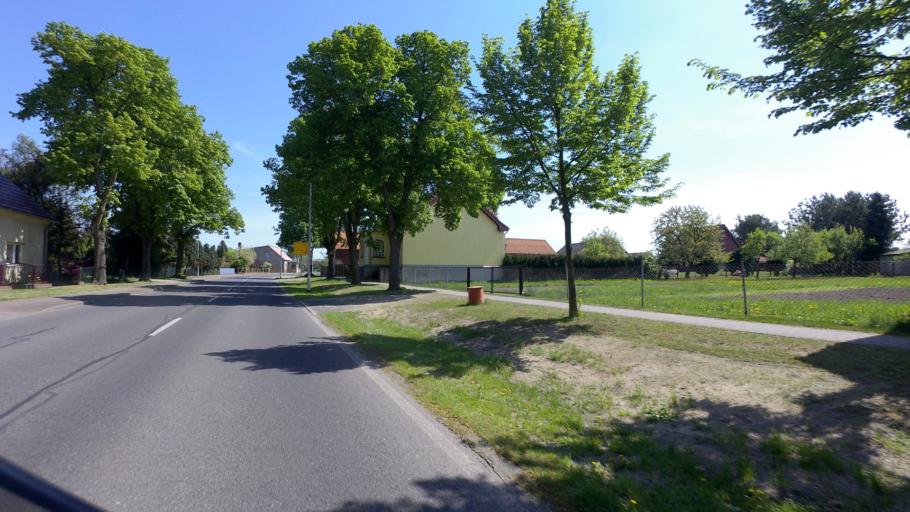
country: DE
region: Brandenburg
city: Schlepzig
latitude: 52.0530
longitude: 13.9995
